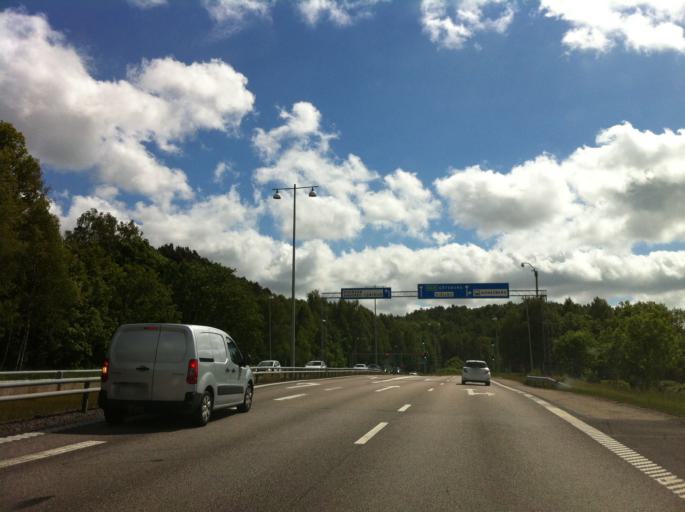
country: SE
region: Vaestra Goetaland
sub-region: Ale Kommun
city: Surte
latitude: 57.8283
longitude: 12.0133
